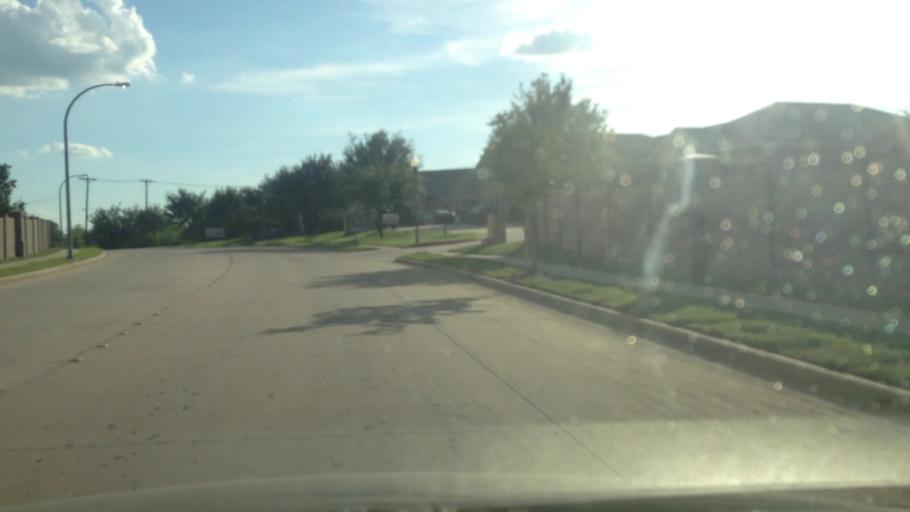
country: US
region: Texas
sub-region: Tarrant County
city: Haslet
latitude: 32.9869
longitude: -97.3959
